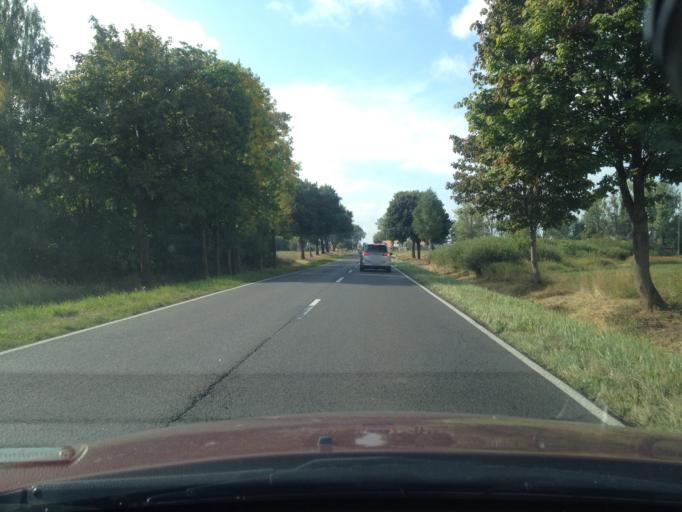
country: PL
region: West Pomeranian Voivodeship
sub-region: Powiat kamienski
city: Kamien Pomorski
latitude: 53.9238
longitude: 14.8079
